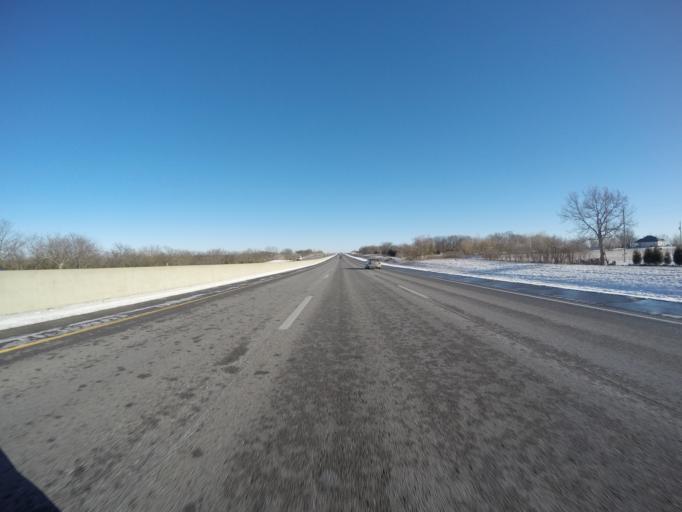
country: US
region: Kansas
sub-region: Shawnee County
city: Topeka
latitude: 39.0096
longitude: -95.4590
